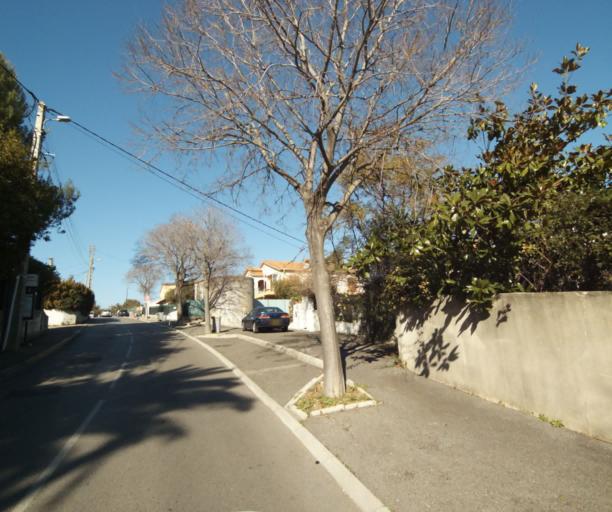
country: FR
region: Provence-Alpes-Cote d'Azur
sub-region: Departement des Alpes-Maritimes
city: Biot
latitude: 43.5998
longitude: 7.1029
